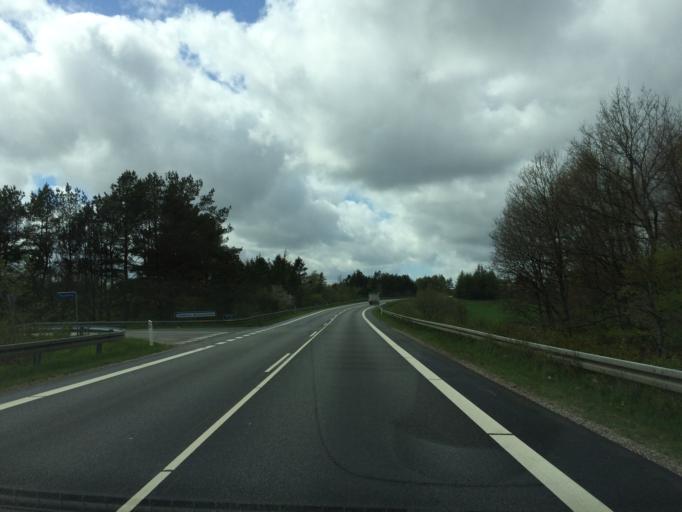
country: DK
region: Central Jutland
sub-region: Viborg Kommune
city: Stoholm
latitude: 56.4359
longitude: 9.2270
